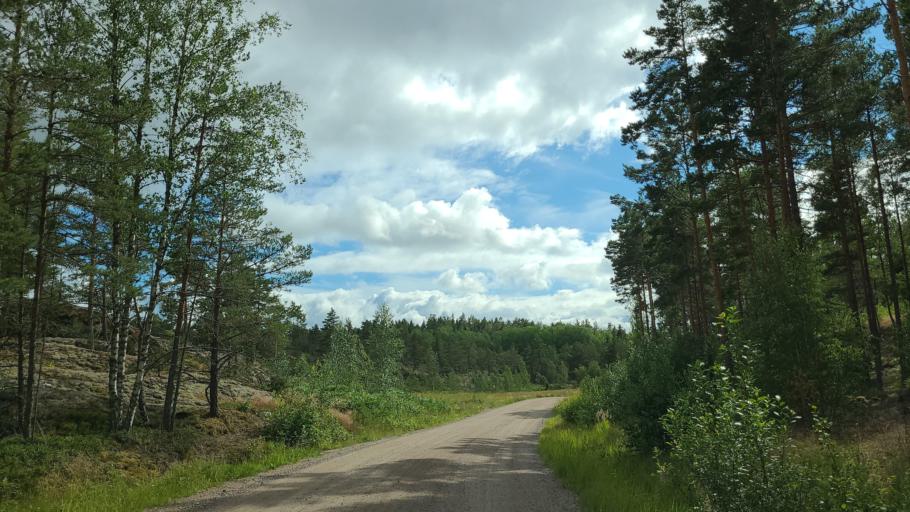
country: FI
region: Varsinais-Suomi
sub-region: Aboland-Turunmaa
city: Nagu
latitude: 60.2015
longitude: 21.7909
